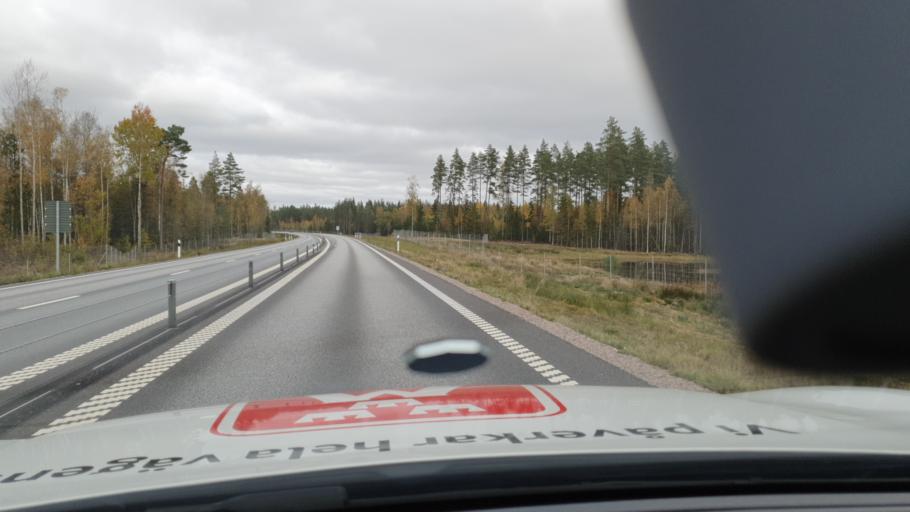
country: SE
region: OErebro
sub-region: Hallsbergs Kommun
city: Palsboda
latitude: 59.0996
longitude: 15.3063
